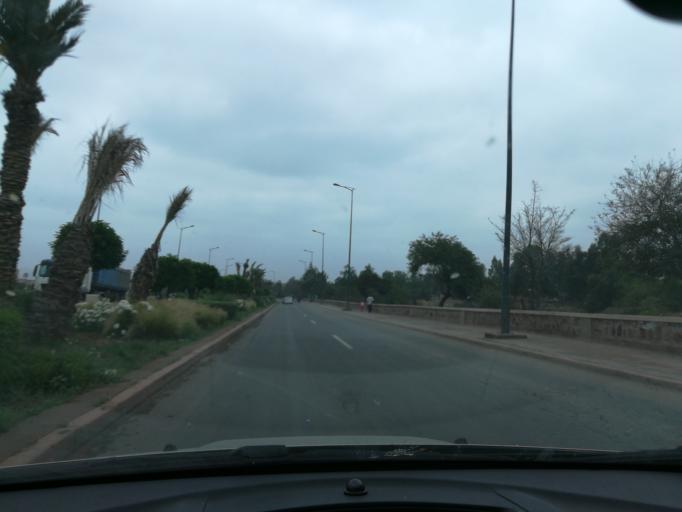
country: MA
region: Marrakech-Tensift-Al Haouz
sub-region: Marrakech
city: Marrakesh
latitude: 31.6570
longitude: -7.9846
